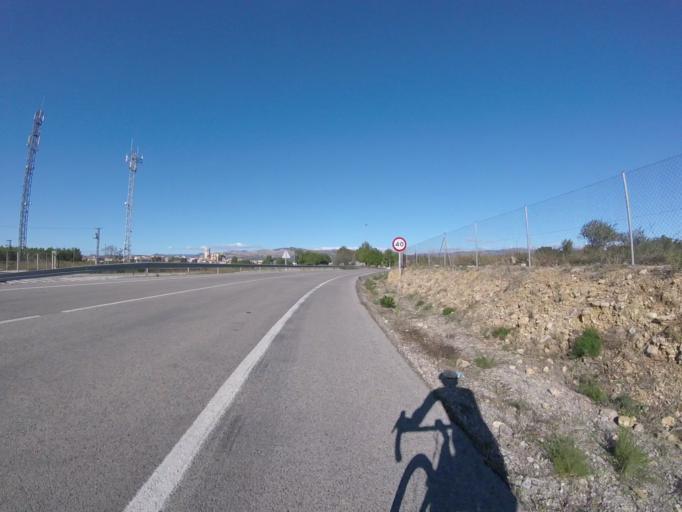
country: ES
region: Valencia
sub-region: Provincia de Castello
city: Chert/Xert
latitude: 40.4653
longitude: 0.1880
